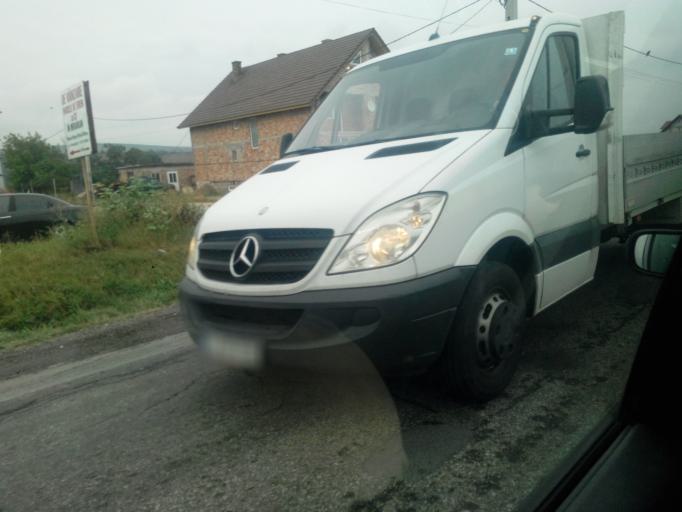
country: RO
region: Cluj
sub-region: Comuna Mihai Viteazu
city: Mihai Viteazu
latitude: 46.5360
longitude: 23.7239
